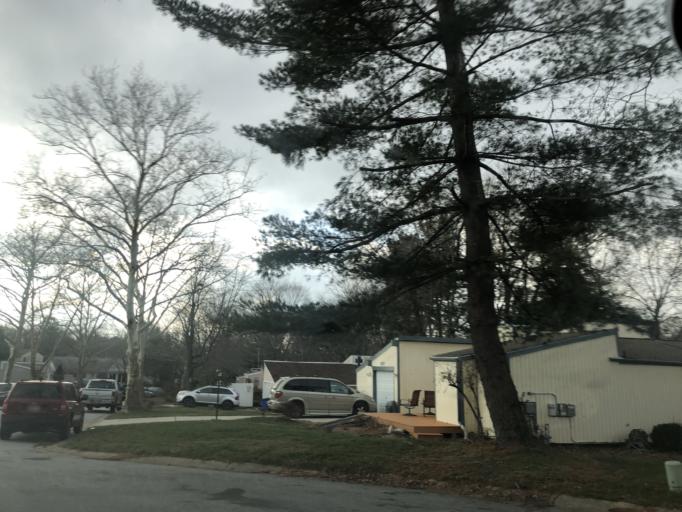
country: US
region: Maryland
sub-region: Howard County
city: Columbia
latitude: 39.2029
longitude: -76.8353
